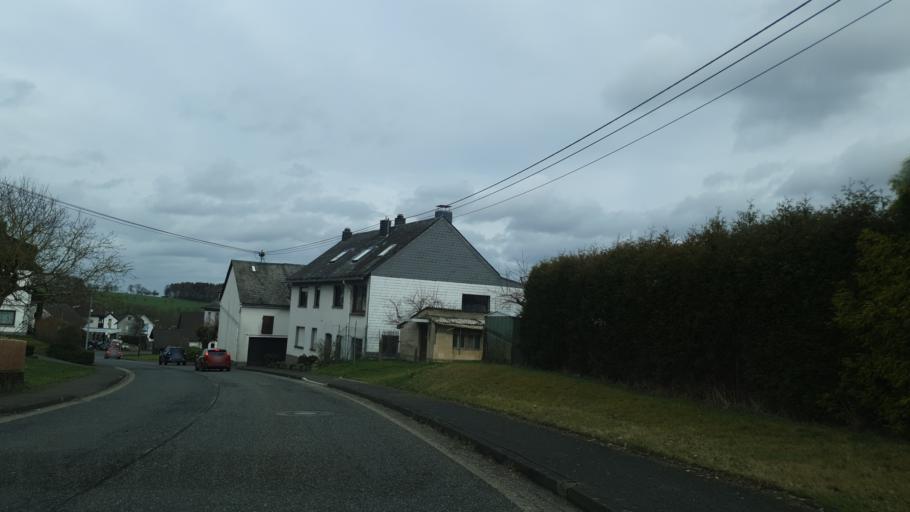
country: DE
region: Rheinland-Pfalz
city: Urbach-Uberdorf
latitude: 50.5561
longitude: 7.5884
